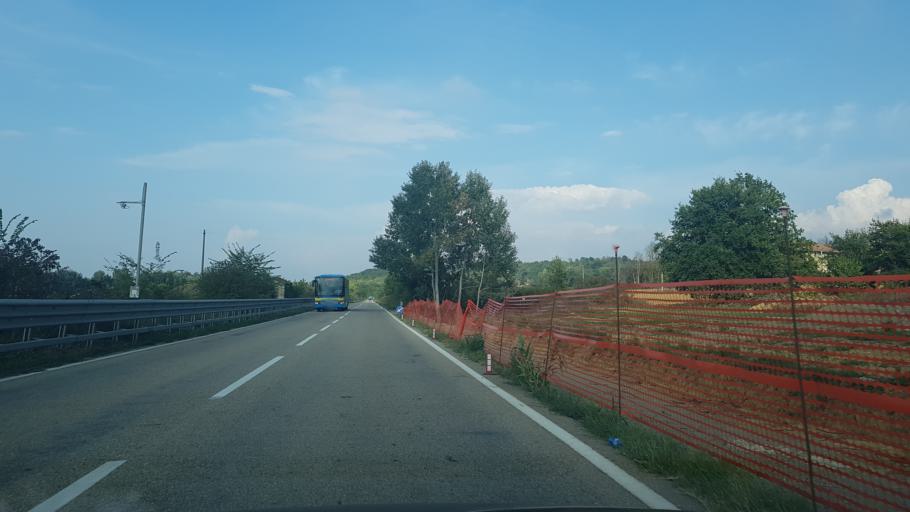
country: IT
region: Piedmont
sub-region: Provincia di Asti
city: Bruno
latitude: 44.8050
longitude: 8.4501
